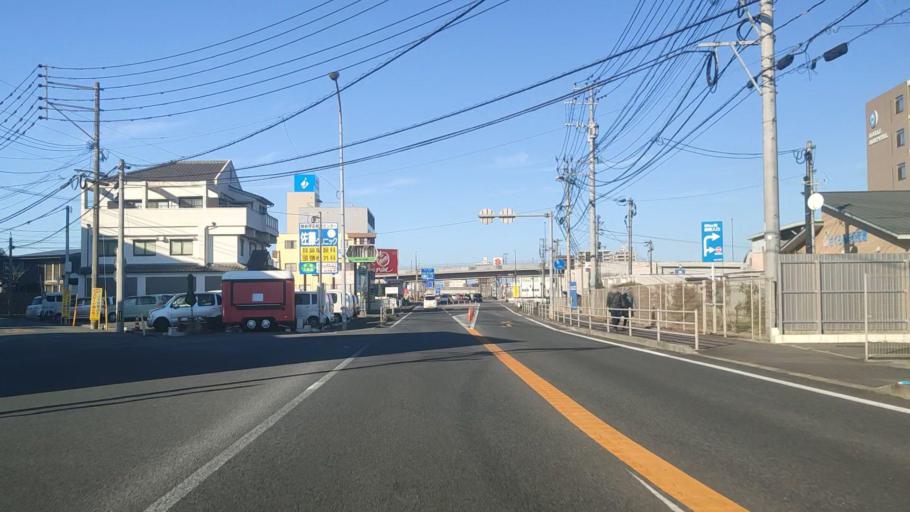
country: JP
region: Oita
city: Oita
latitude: 33.2241
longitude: 131.6187
